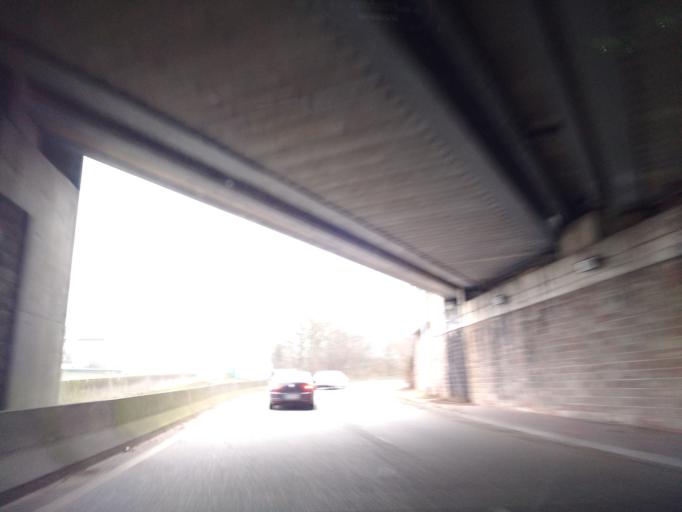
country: FR
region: Alsace
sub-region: Departement du Bas-Rhin
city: Strasbourg
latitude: 48.5708
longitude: 7.7403
